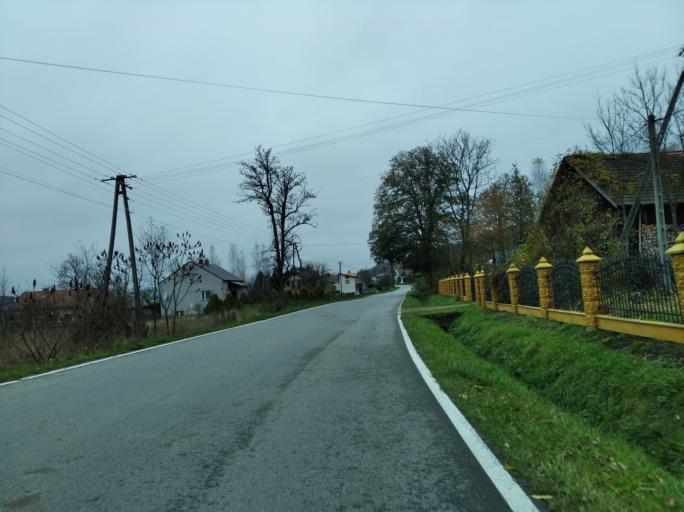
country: PL
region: Subcarpathian Voivodeship
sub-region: Powiat krosnienski
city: Leki
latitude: 49.8220
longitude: 21.6447
